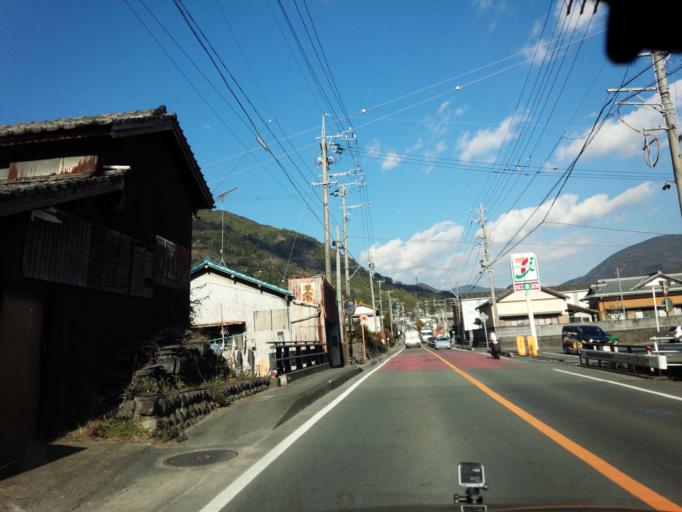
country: JP
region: Shizuoka
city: Shizuoka-shi
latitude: 35.0808
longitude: 138.5150
